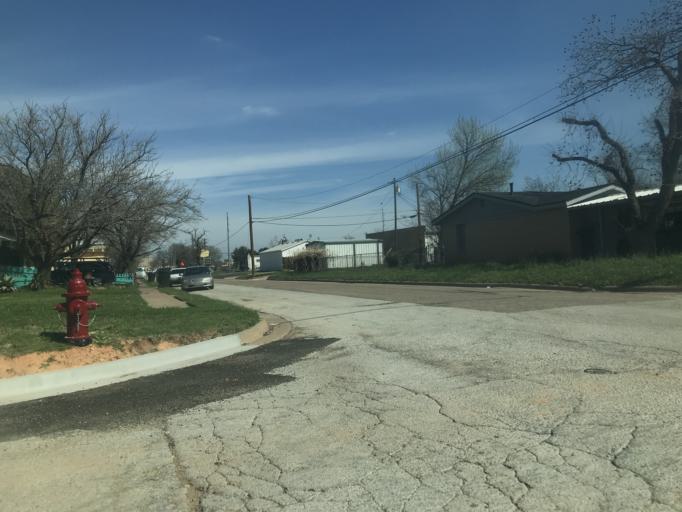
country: US
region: Texas
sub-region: Taylor County
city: Abilene
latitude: 32.4490
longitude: -99.7659
